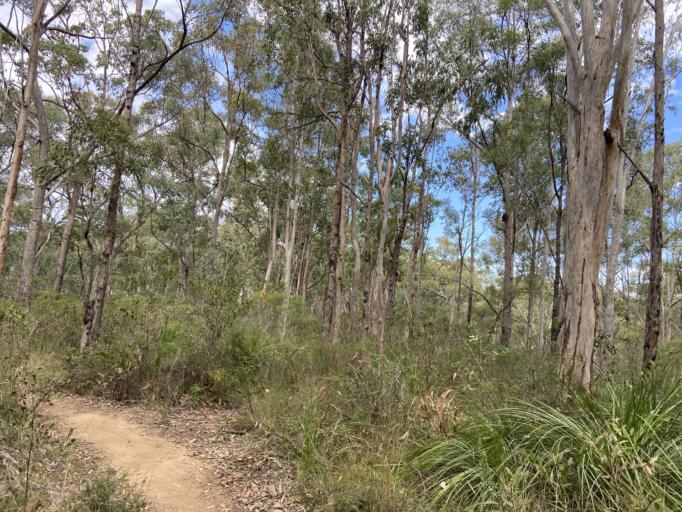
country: AU
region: Queensland
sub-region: Moreton Bay
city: Caboolture
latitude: -26.9476
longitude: 152.9545
